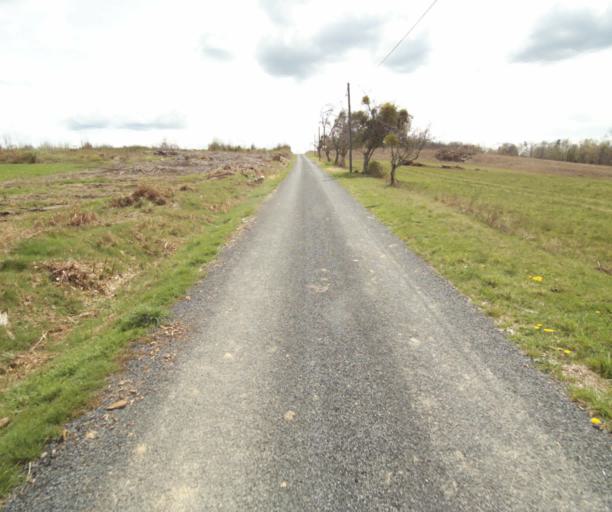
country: FR
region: Limousin
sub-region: Departement de la Correze
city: Laguenne
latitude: 45.2363
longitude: 1.8726
